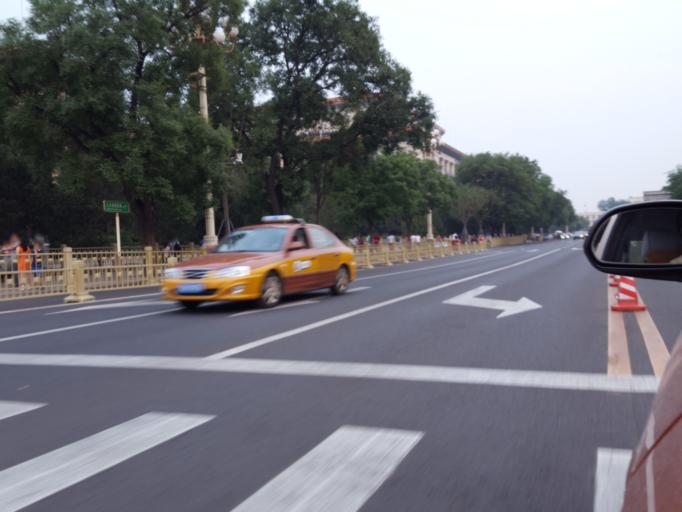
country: CN
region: Beijing
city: Beijing
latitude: 39.9059
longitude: 116.3854
